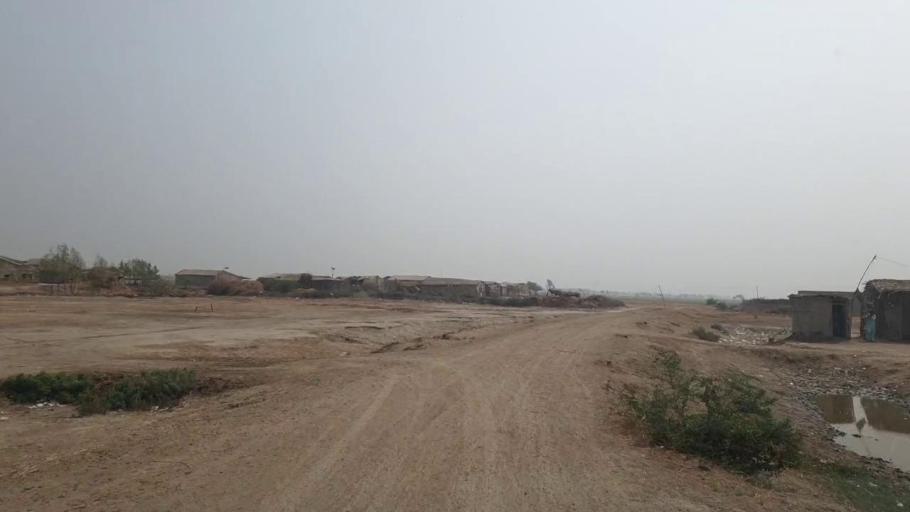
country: PK
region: Sindh
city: Kario
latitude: 24.6449
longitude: 68.6073
